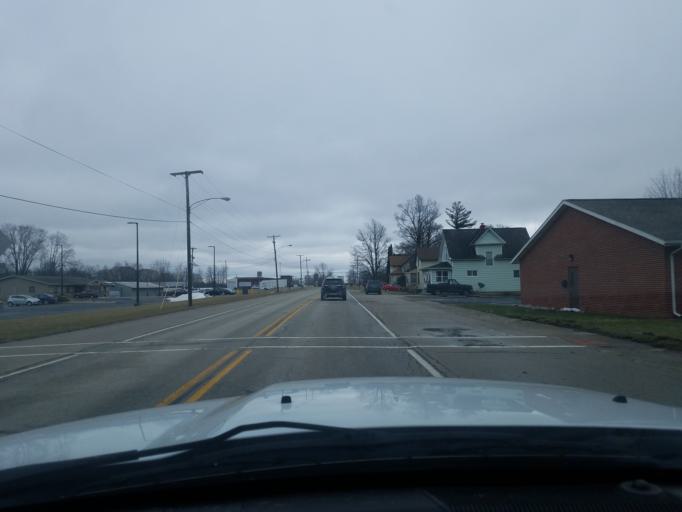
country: US
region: Indiana
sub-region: Noble County
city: Albion
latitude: 41.3959
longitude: -85.4149
